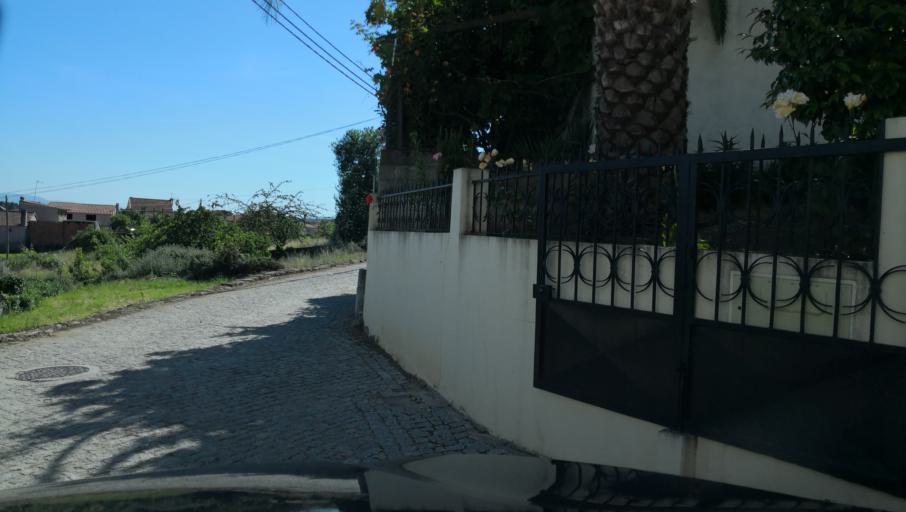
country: PT
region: Vila Real
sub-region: Vila Real
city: Vila Real
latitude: 41.2834
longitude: -7.6951
